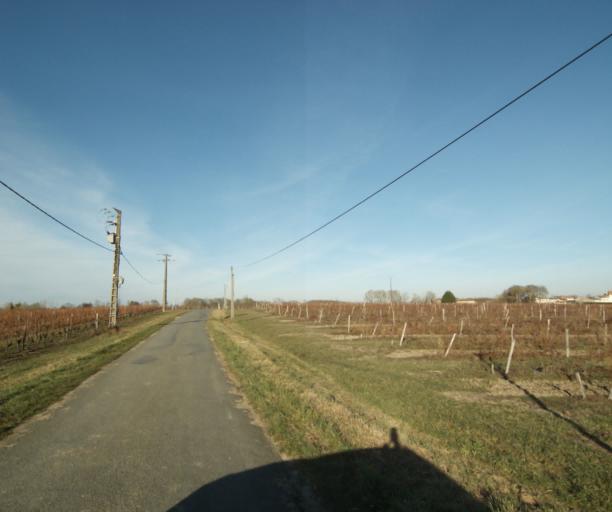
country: FR
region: Poitou-Charentes
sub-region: Departement de la Charente-Maritime
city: Burie
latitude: 45.7849
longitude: -0.4173
